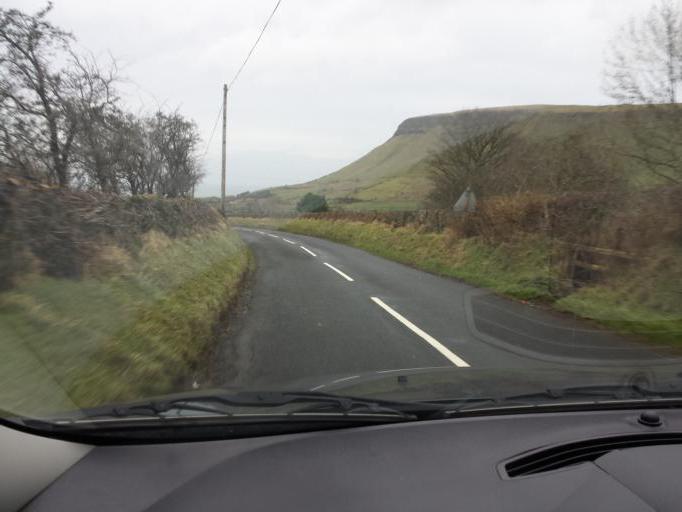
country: GB
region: Northern Ireland
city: Glenariff
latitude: 55.0661
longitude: -6.1062
